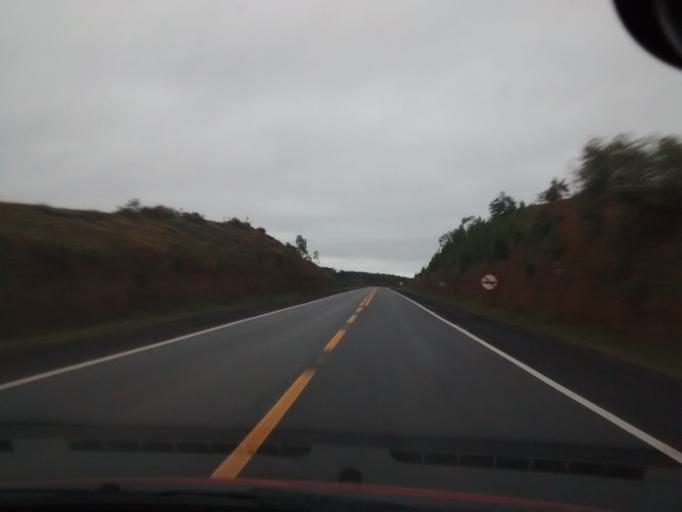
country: BR
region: Rio Grande do Sul
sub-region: Vacaria
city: Estrela
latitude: -28.1633
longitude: -50.6669
